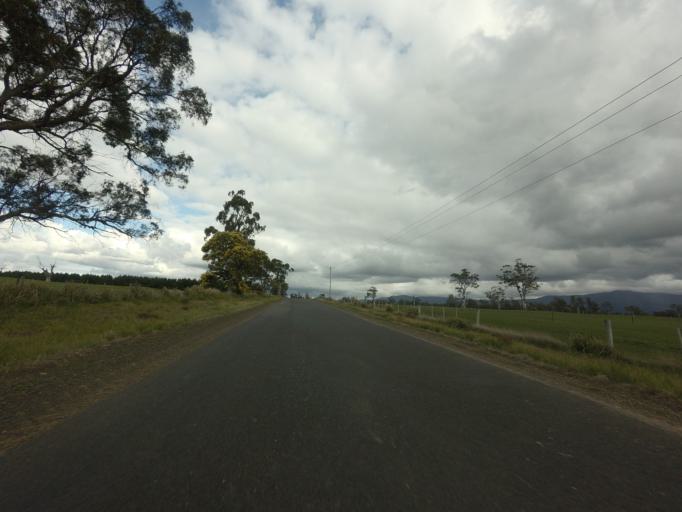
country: AU
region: Tasmania
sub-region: Northern Midlands
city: Longford
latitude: -41.7614
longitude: 147.0830
